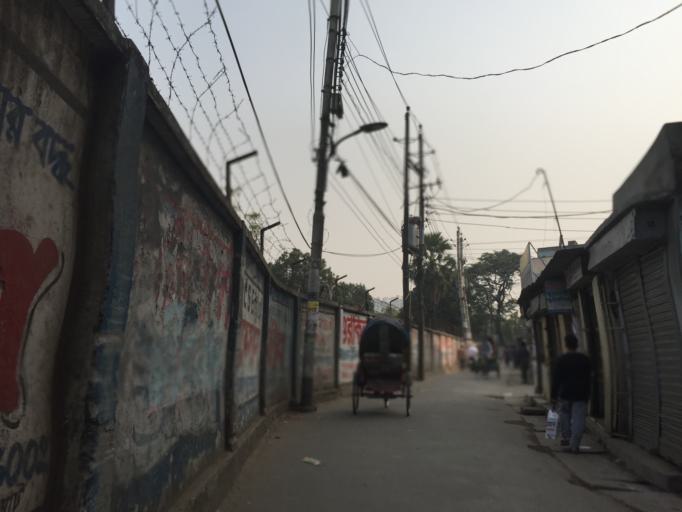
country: BD
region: Dhaka
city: Azimpur
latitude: 23.7307
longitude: 90.3810
